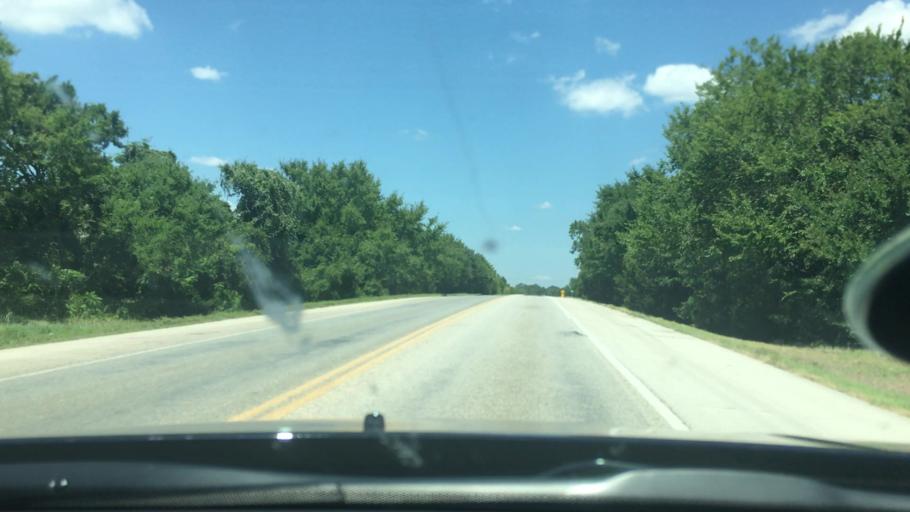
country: US
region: Oklahoma
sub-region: Marshall County
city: Oakland
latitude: 34.1784
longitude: -96.8625
